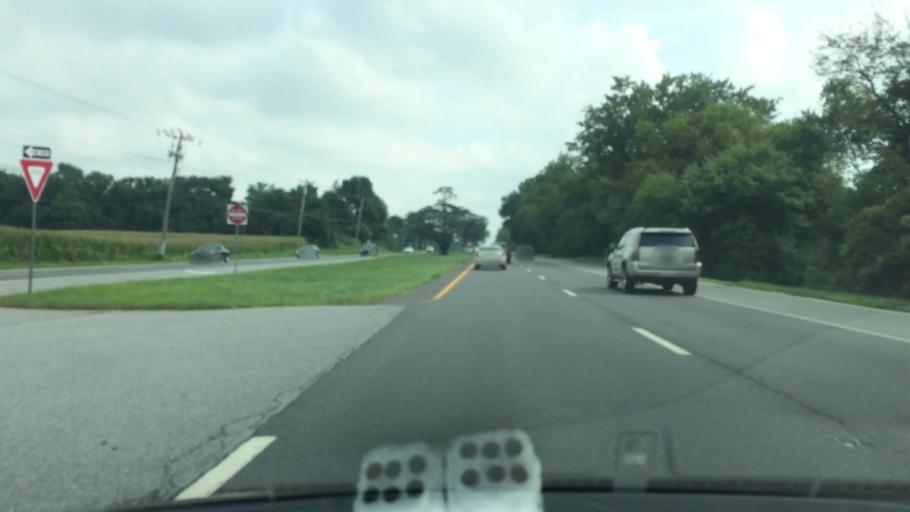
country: US
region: Delaware
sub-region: New Castle County
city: Bear
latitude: 39.6327
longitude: -75.6328
